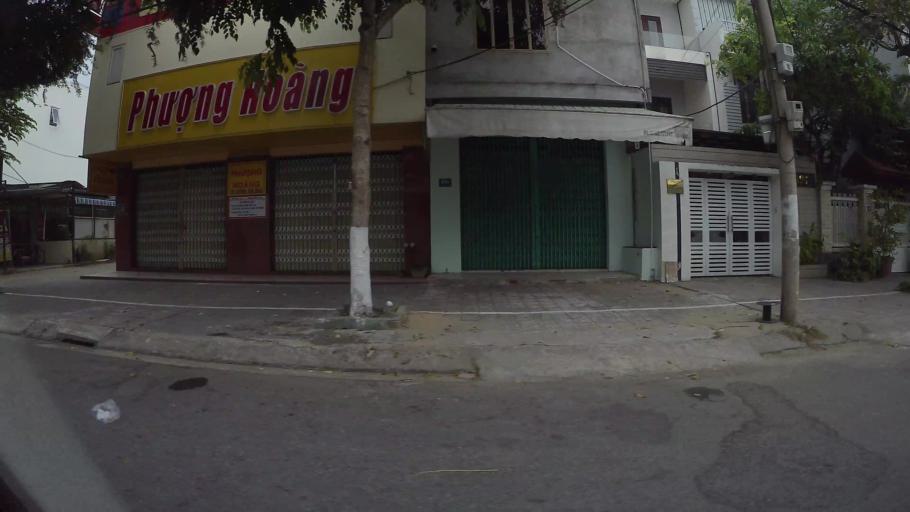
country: VN
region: Da Nang
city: Cam Le
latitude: 16.0335
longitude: 108.2146
